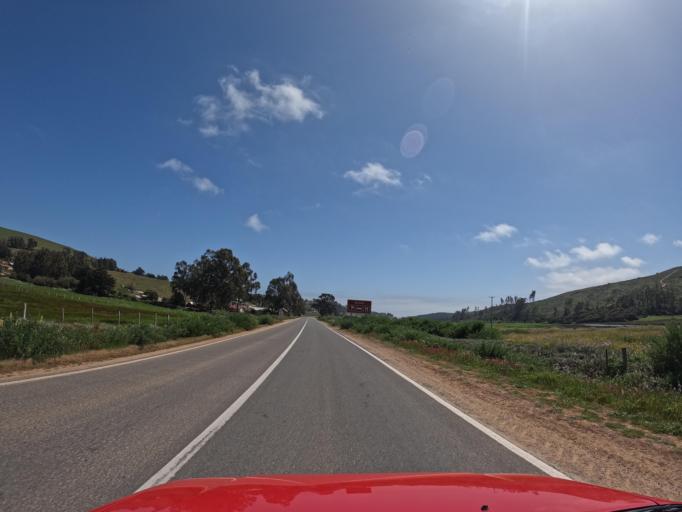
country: CL
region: O'Higgins
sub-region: Provincia de Colchagua
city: Santa Cruz
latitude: -34.6526
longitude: -72.0233
